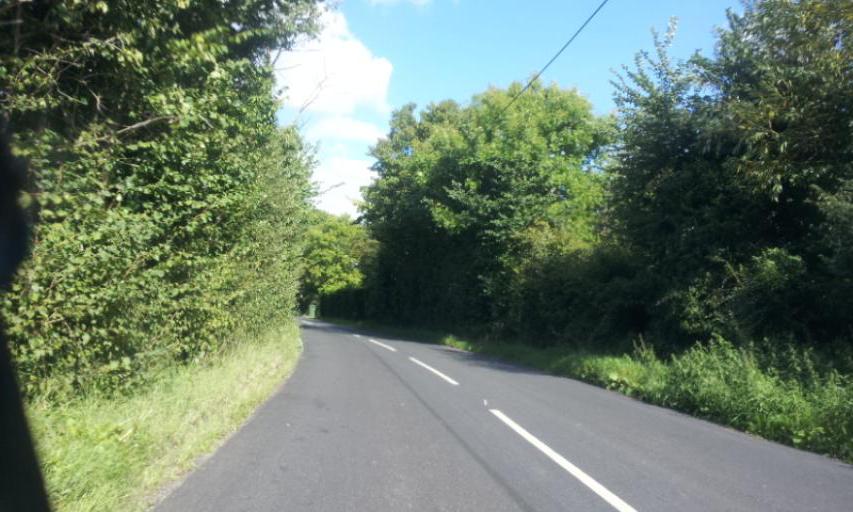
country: GB
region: England
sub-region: Kent
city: Marden
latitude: 51.1727
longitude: 0.5081
